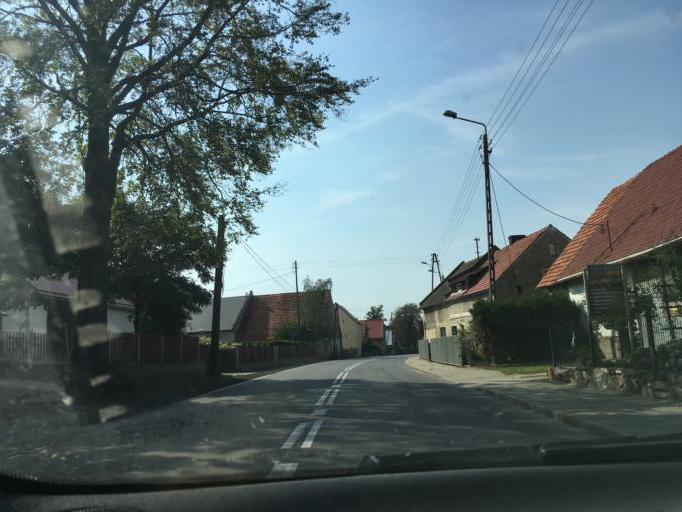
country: PL
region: Opole Voivodeship
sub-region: Powiat nyski
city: Nysa
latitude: 50.4244
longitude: 17.4353
